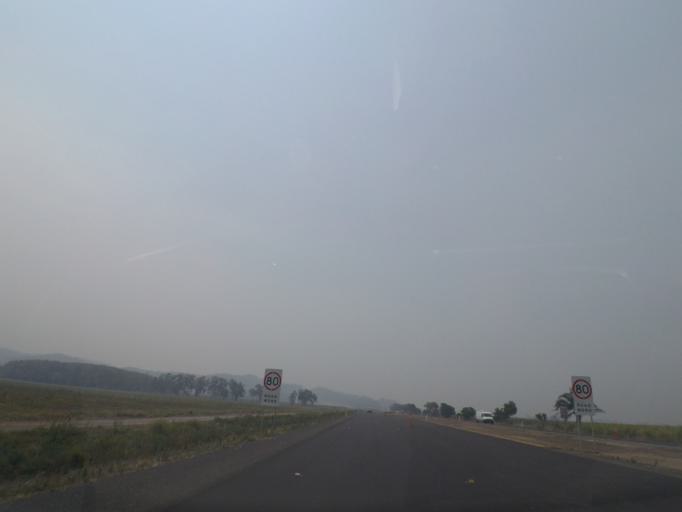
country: AU
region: New South Wales
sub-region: Ballina
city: Ballina
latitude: -28.8950
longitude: 153.4812
